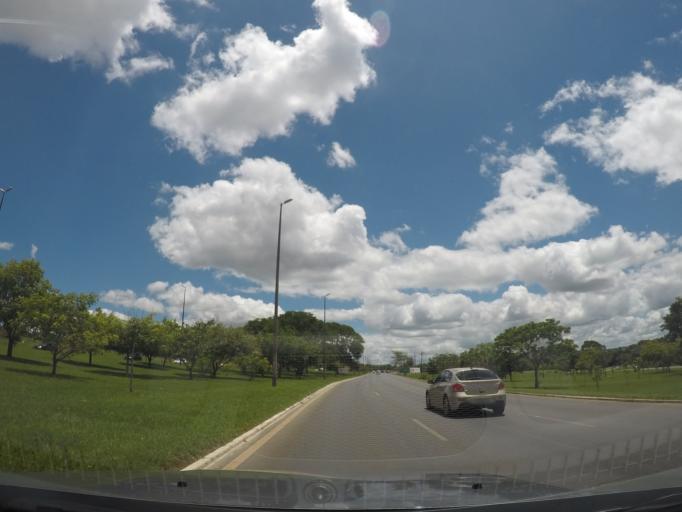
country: BR
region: Federal District
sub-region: Brasilia
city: Brasilia
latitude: -15.8205
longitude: -47.8818
